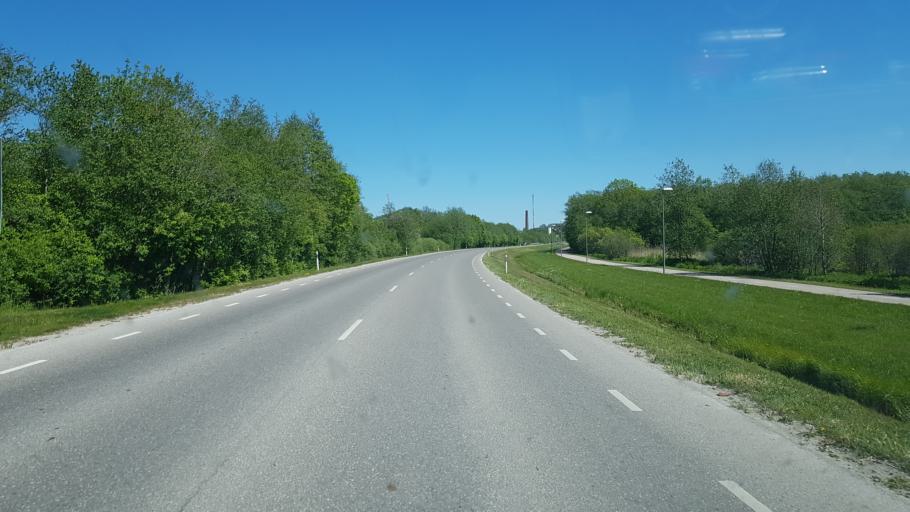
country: EE
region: Saare
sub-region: Kuressaare linn
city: Kuressaare
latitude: 58.2696
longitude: 22.4733
